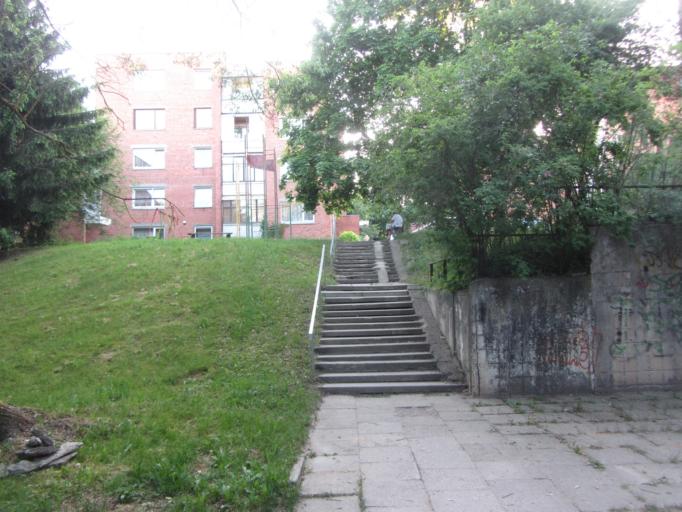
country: LT
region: Vilnius County
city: Seskine
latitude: 54.7273
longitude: 25.2758
